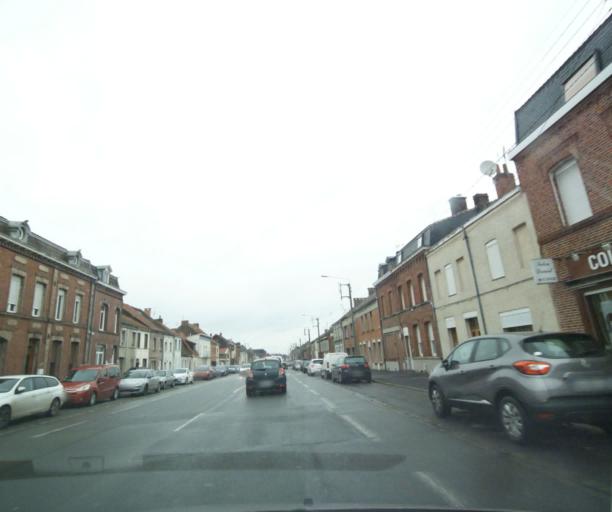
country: FR
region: Nord-Pas-de-Calais
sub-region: Departement du Nord
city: Beuvrages
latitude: 50.3800
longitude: 3.4946
